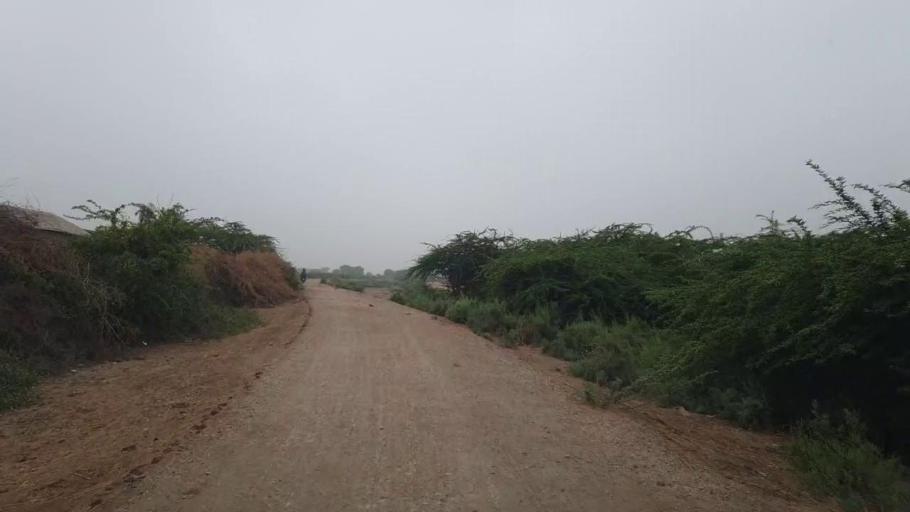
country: PK
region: Sindh
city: Badin
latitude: 24.6044
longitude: 68.6748
